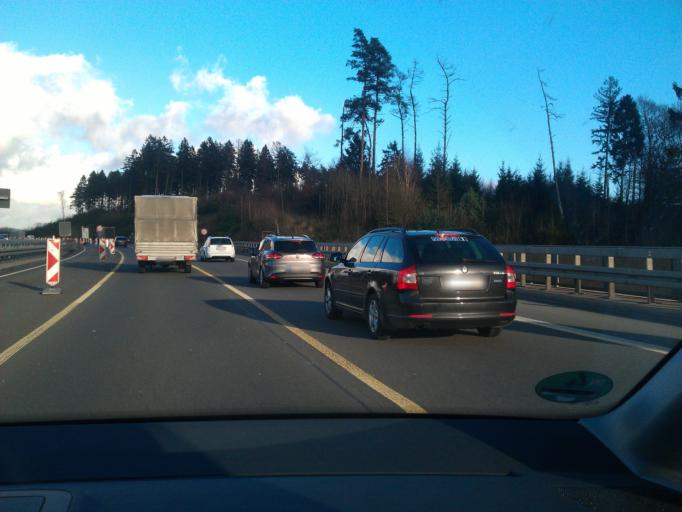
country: DE
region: North Rhine-Westphalia
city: Wermelskirchen
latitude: 51.1438
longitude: 7.2000
